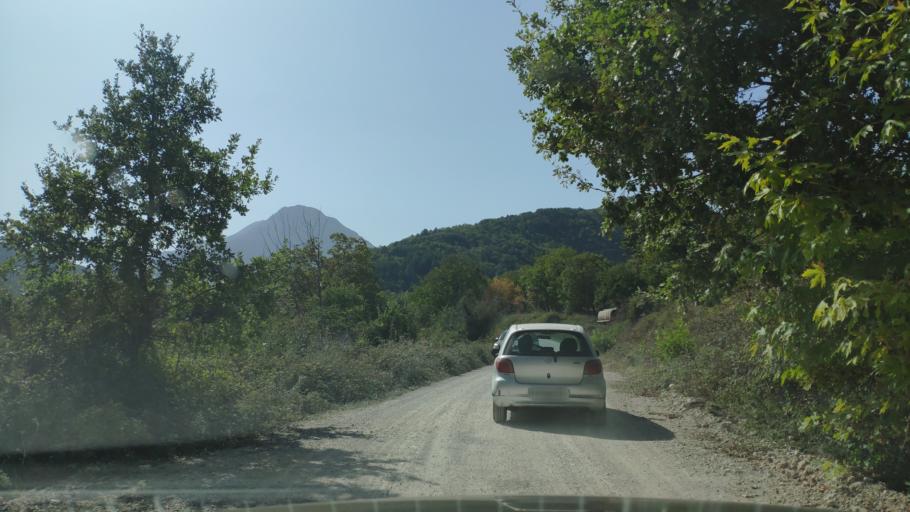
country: GR
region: West Greece
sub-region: Nomos Achaias
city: Aiyira
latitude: 37.9459
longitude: 22.3219
